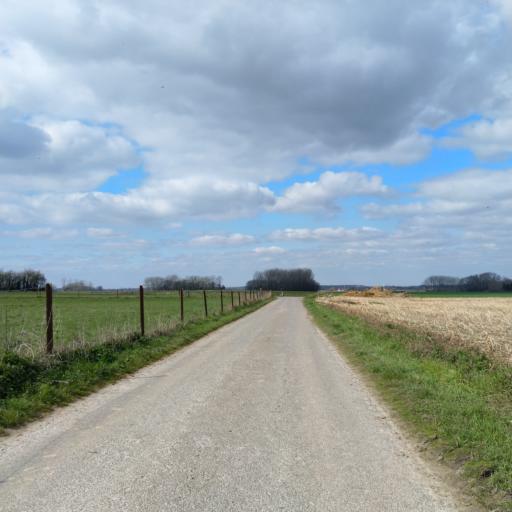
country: BE
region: Wallonia
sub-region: Province du Hainaut
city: Jurbise
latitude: 50.5407
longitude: 3.9558
